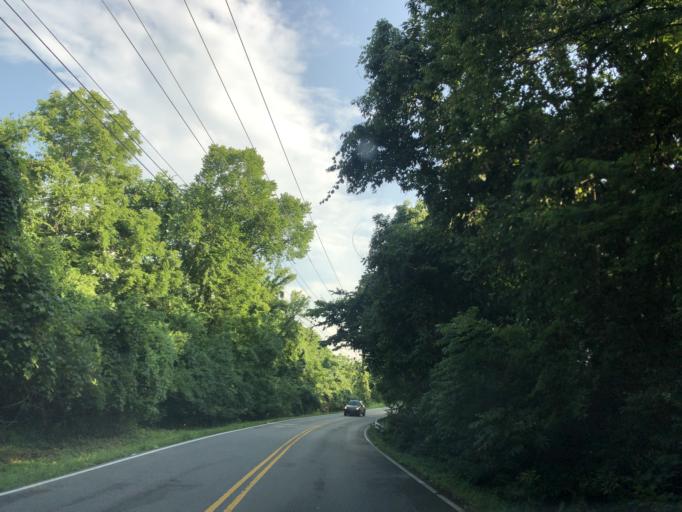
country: US
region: Tennessee
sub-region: Davidson County
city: Lakewood
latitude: 36.1502
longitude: -86.6473
